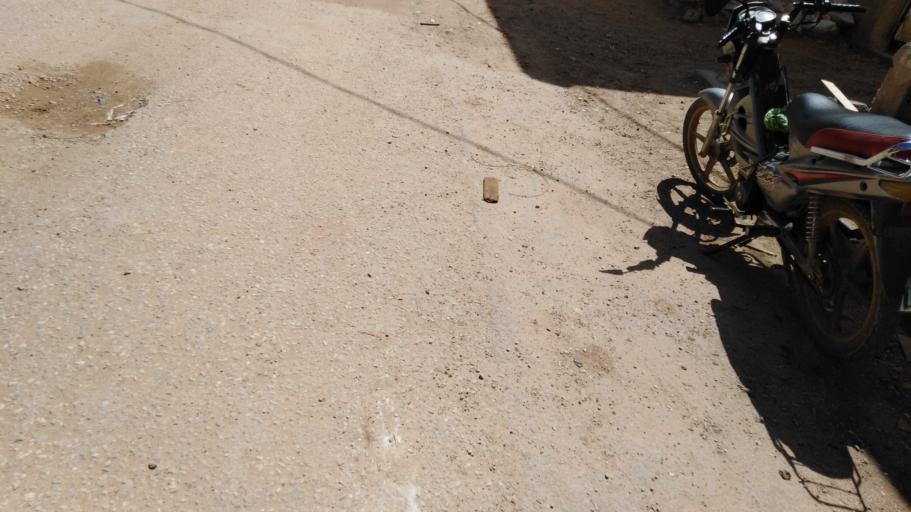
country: TN
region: Safaqis
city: Sfax
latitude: 34.7410
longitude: 10.5305
